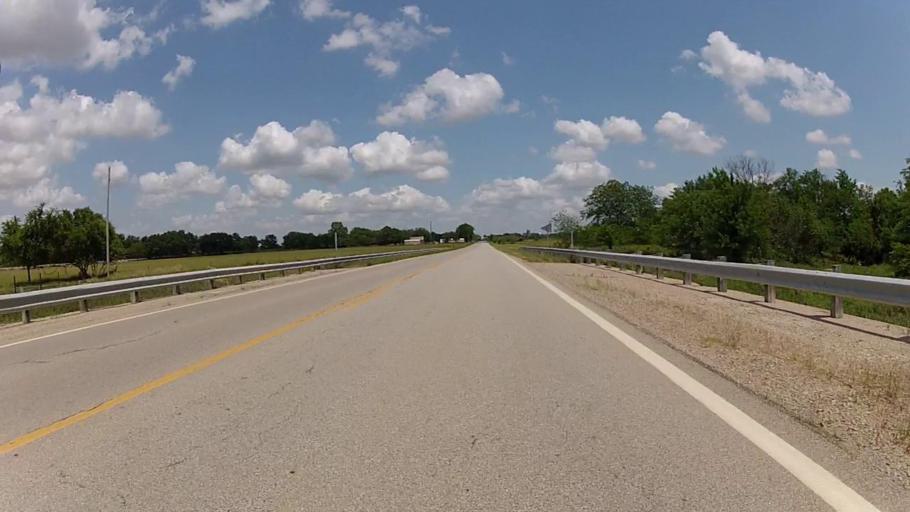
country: US
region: Kansas
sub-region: Labette County
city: Altamont
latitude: 37.1932
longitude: -95.3212
